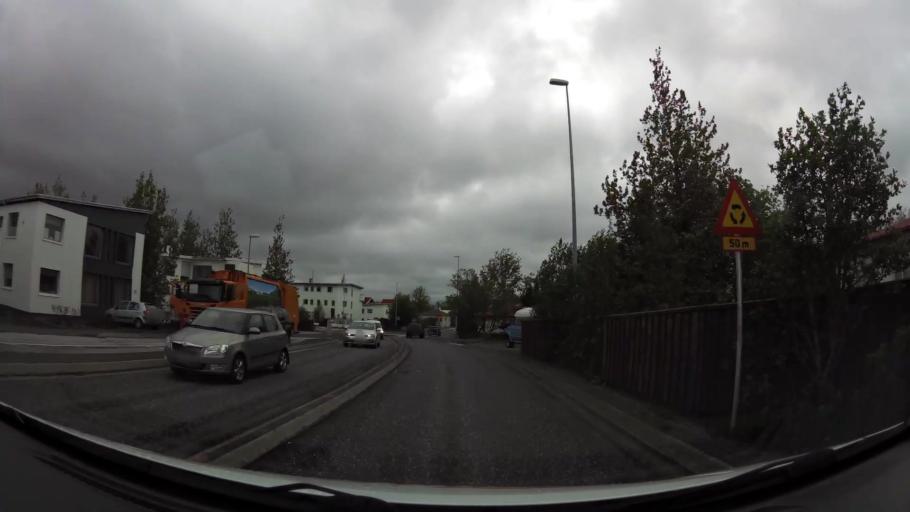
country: IS
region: Capital Region
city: Hafnarfjoerdur
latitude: 64.0738
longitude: -21.9530
